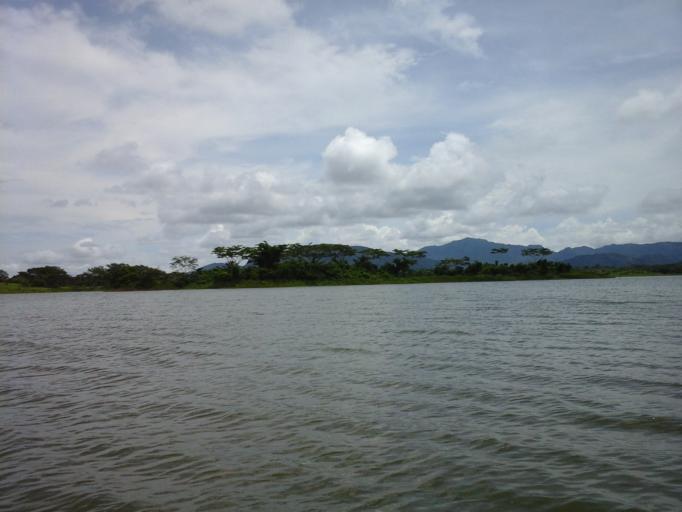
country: CO
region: Bolivar
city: San Cristobal
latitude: 9.8766
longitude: -75.3033
